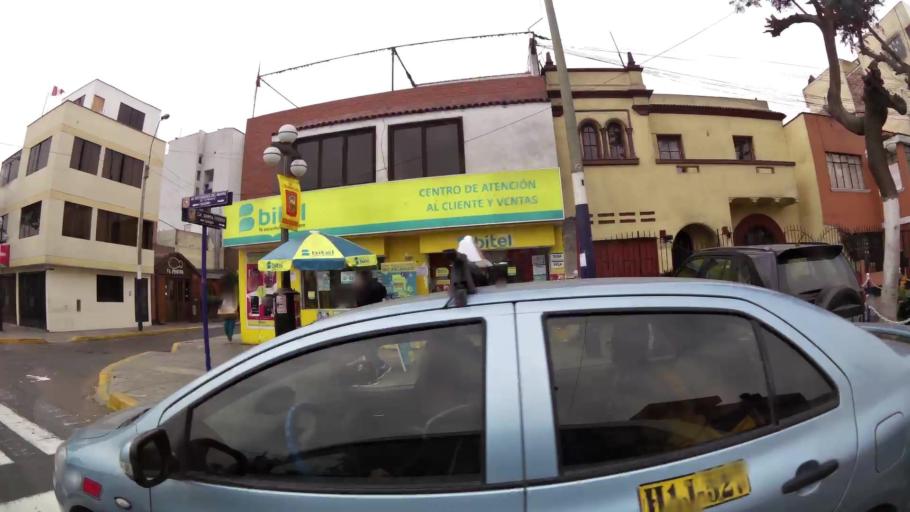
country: PE
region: Lima
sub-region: Lima
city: Surco
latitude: -12.1669
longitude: -77.0262
